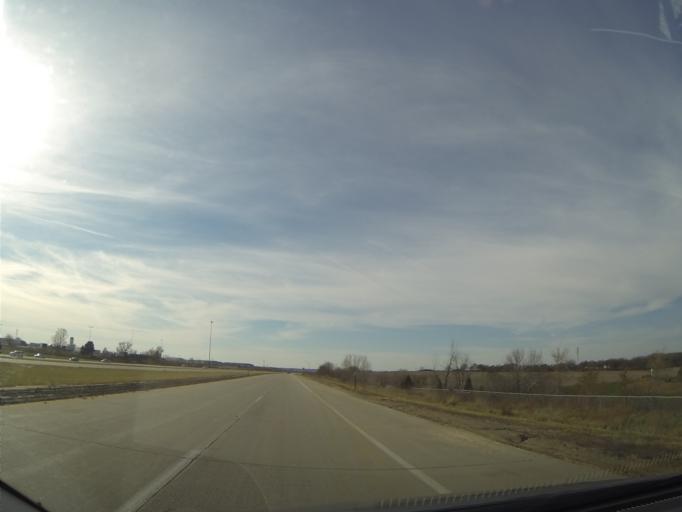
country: US
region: Nebraska
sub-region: Sarpy County
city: Gretna
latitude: 41.0948
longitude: -96.2554
